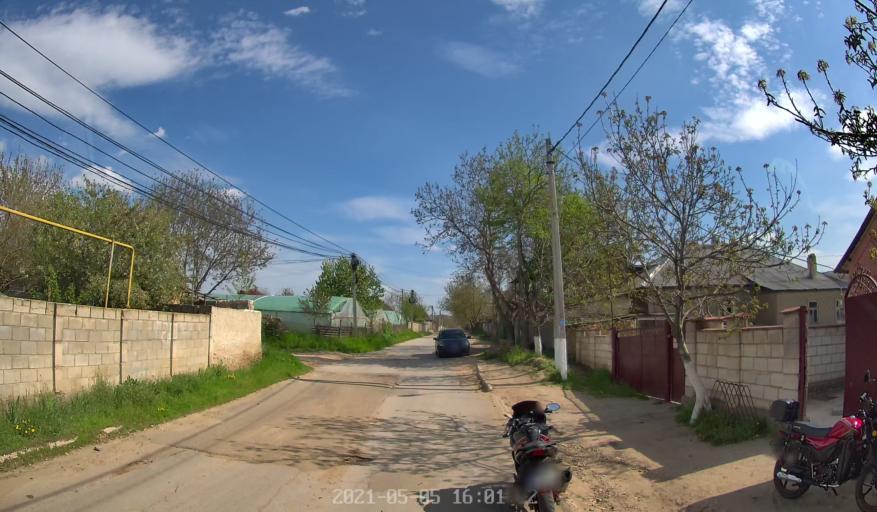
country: MD
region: Criuleni
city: Criuleni
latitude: 47.1440
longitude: 29.1998
